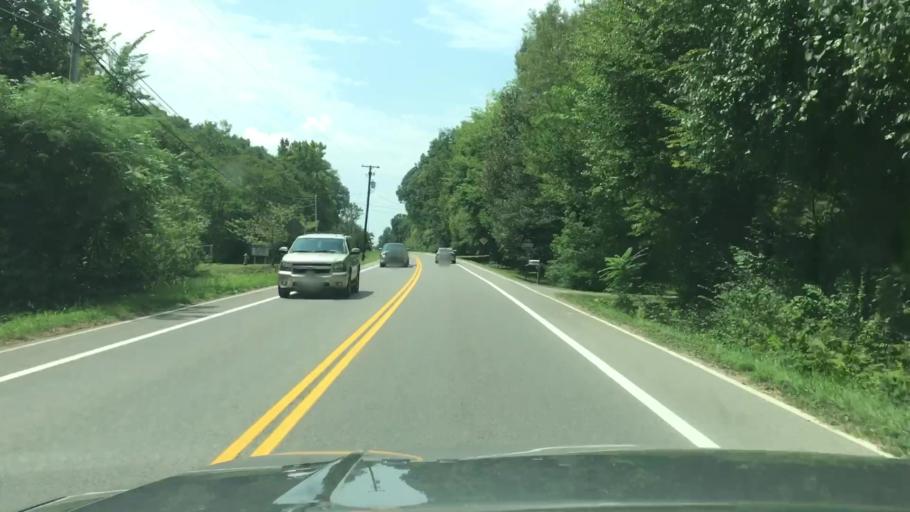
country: US
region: Tennessee
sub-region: Davidson County
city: Forest Hills
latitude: 36.0249
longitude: -86.8810
